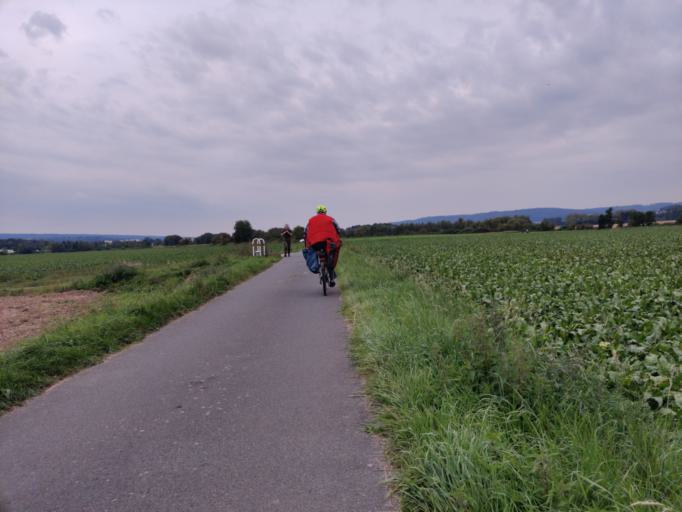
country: DE
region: Lower Saxony
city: Holzminden
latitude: 51.8502
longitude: 9.4591
